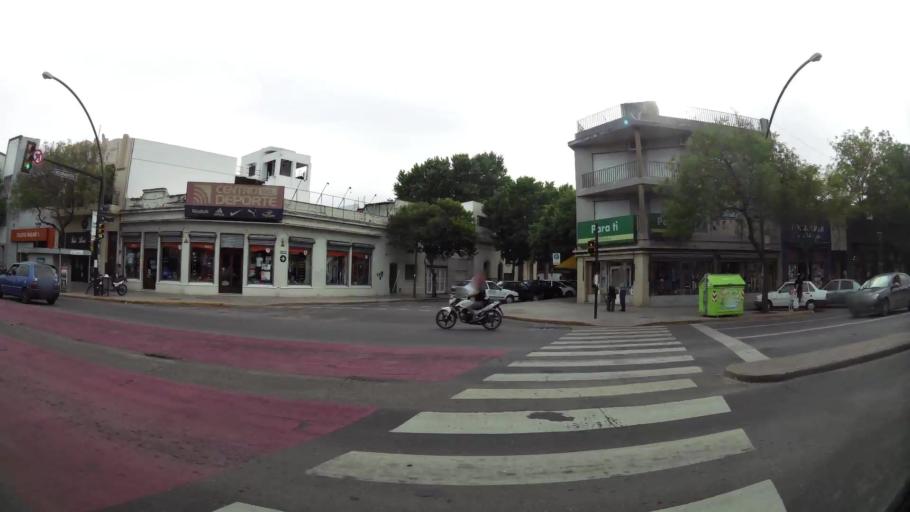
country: AR
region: Santa Fe
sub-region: Departamento de Rosario
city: Rosario
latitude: -32.9180
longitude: -60.6834
